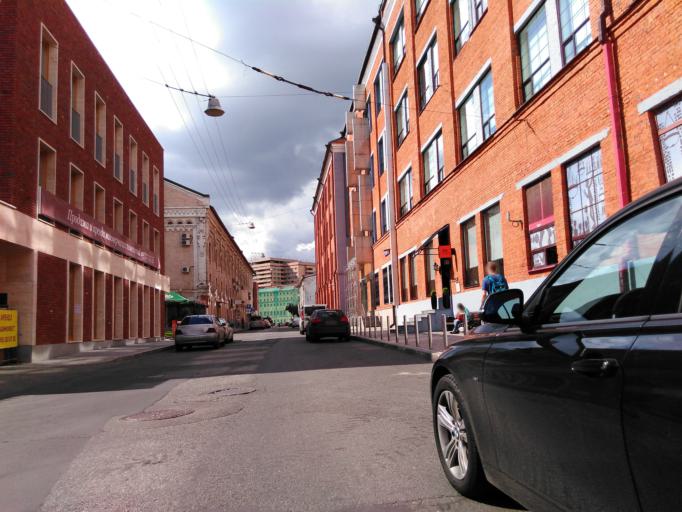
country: RU
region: Moskovskaya
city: Dorogomilovo
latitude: 55.7349
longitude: 37.5854
